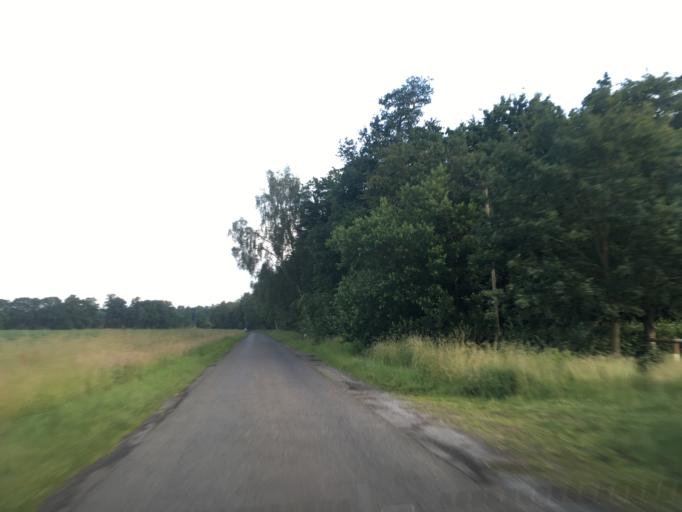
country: DE
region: North Rhine-Westphalia
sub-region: Regierungsbezirk Munster
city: Senden
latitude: 51.9104
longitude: 7.5419
